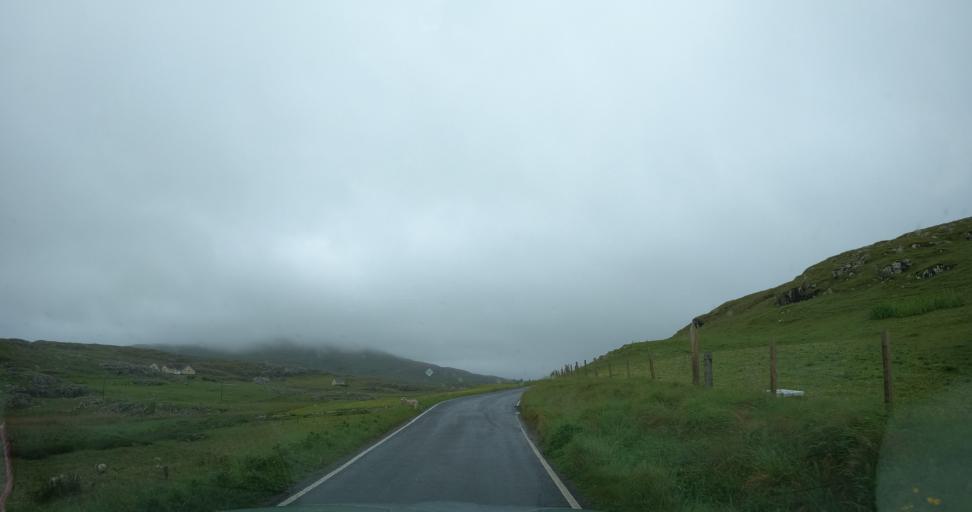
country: GB
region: Scotland
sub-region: Eilean Siar
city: Barra
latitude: 57.0031
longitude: -7.4956
